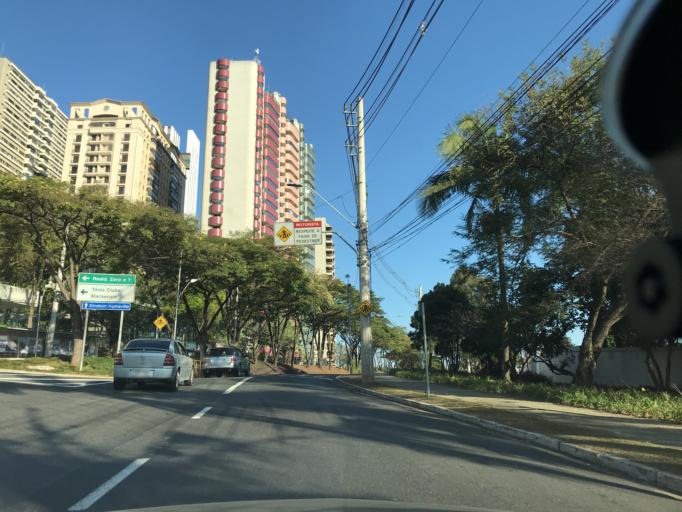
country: BR
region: Sao Paulo
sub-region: Barueri
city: Barueri
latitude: -23.4933
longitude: -46.8536
